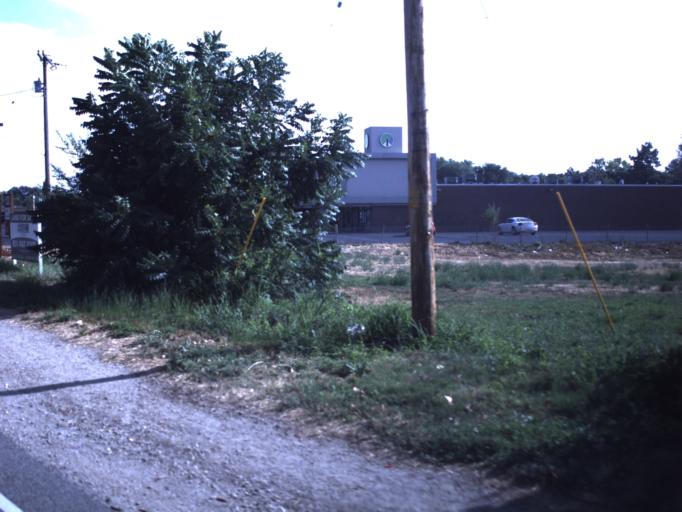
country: US
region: Utah
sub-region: Weber County
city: Harrisville
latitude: 41.2626
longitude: -111.9720
